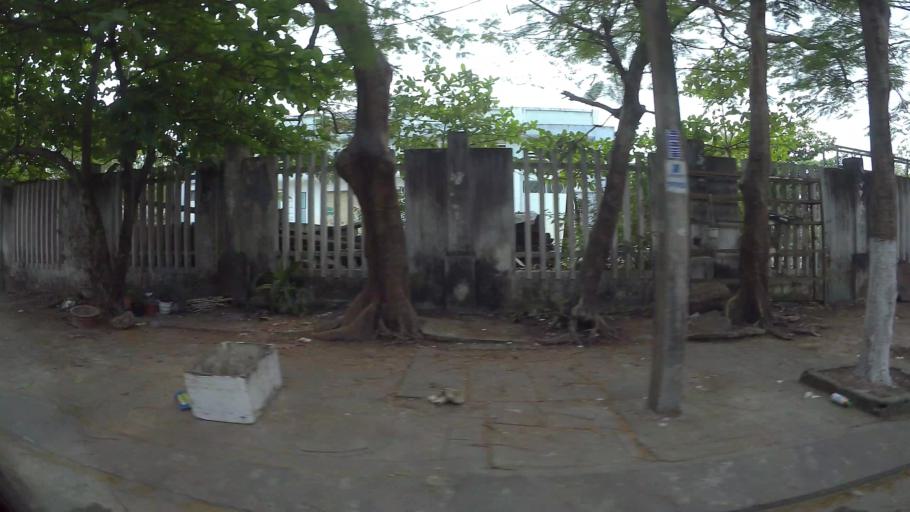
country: VN
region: Da Nang
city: Lien Chieu
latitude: 16.0785
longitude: 108.1687
